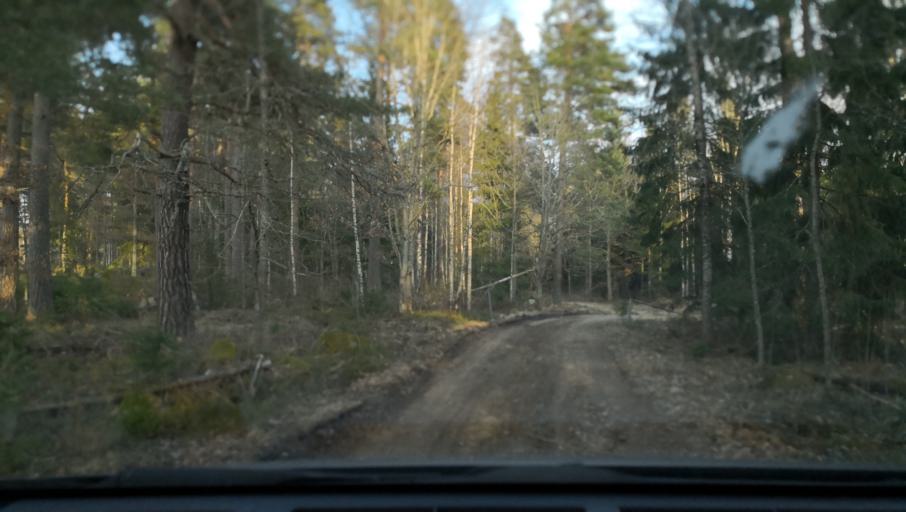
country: SE
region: OErebro
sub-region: Orebro Kommun
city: Hovsta
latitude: 59.3936
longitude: 15.2704
